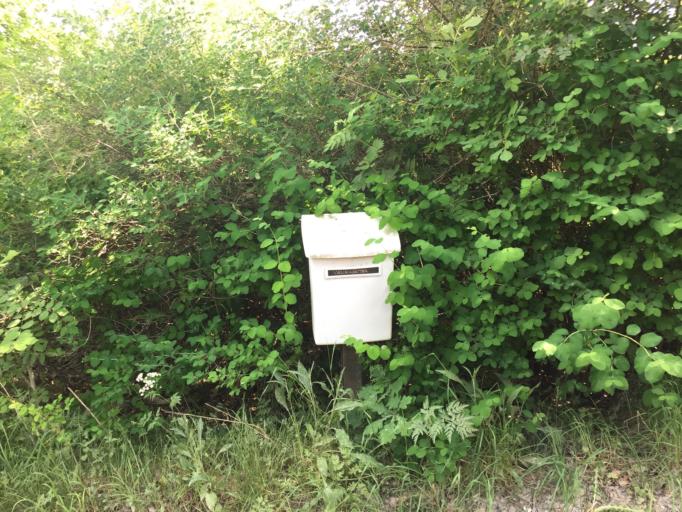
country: SE
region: Soedermanland
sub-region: Flens Kommun
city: Halleforsnas
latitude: 59.0732
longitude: 16.4774
